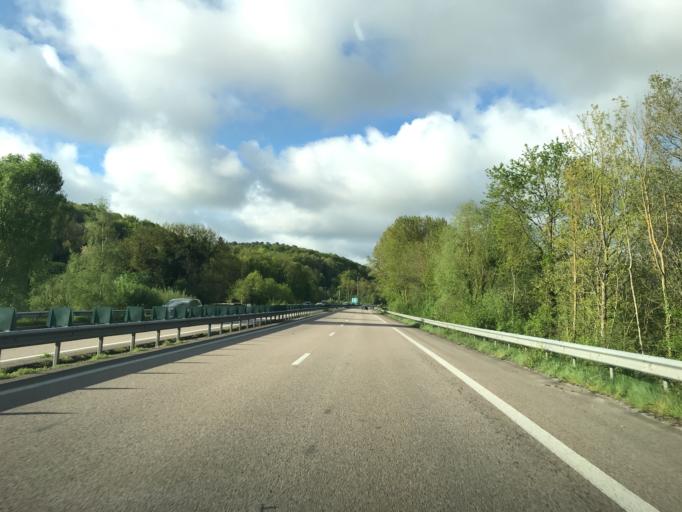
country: FR
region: Haute-Normandie
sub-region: Departement de l'Eure
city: Toutainville
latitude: 49.3622
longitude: 0.4664
